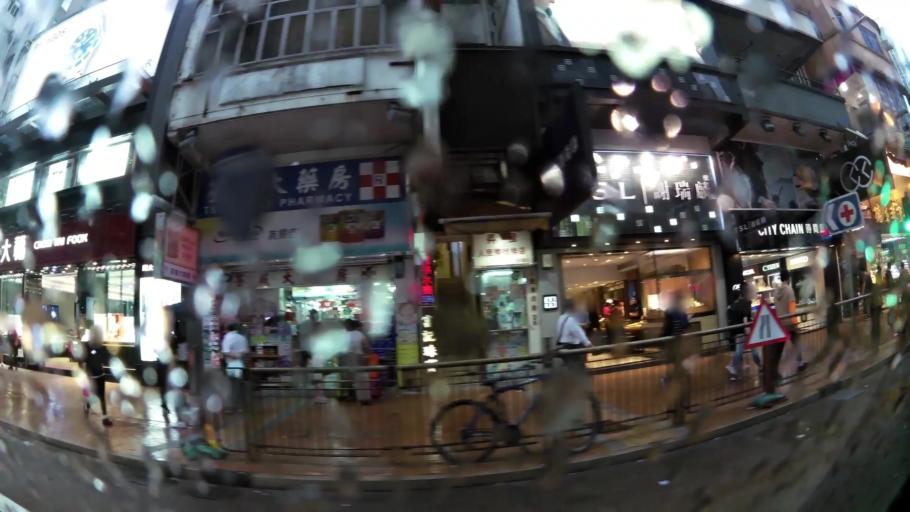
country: HK
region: Tsuen Wan
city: Tsuen Wan
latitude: 22.3701
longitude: 114.1171
